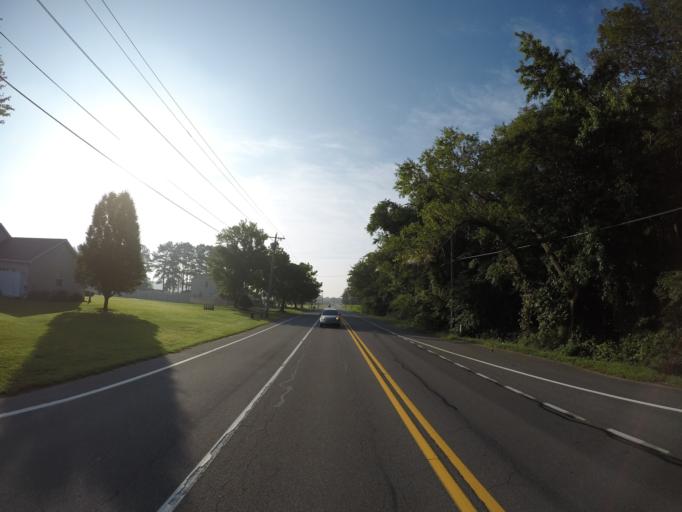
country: US
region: Delaware
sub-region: Sussex County
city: Selbyville
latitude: 38.5427
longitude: -75.2246
